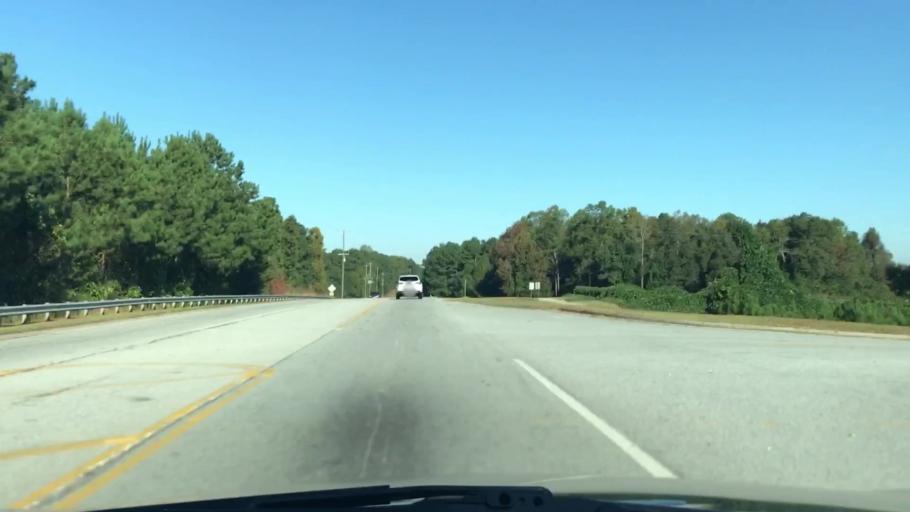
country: US
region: Georgia
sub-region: Carroll County
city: Villa Rica
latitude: 33.7337
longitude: -84.9015
